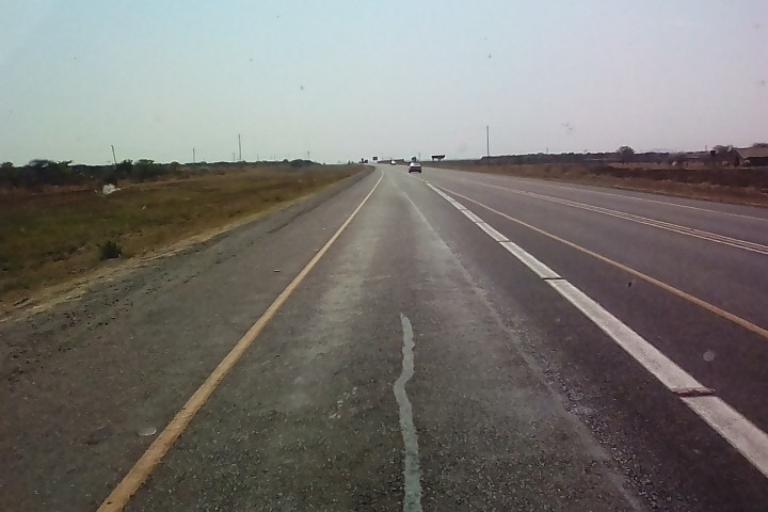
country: ZA
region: North-West
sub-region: Bojanala Platinum District Municipality
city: Brits
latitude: -25.6678
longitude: 27.8521
